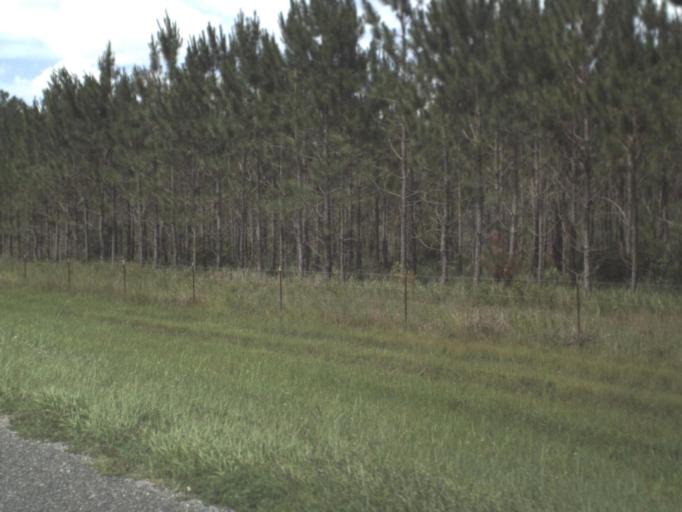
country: US
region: Florida
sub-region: Clay County
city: Middleburg
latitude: 29.9878
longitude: -81.8977
